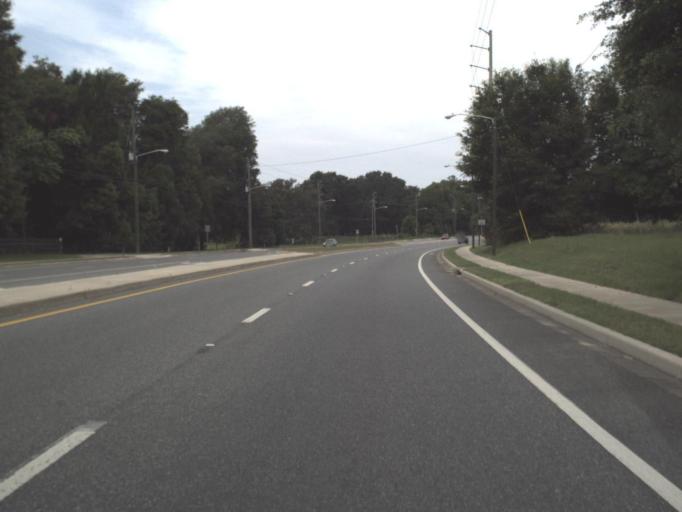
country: US
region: Florida
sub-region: Putnam County
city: Palatka
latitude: 29.6303
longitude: -81.7220
